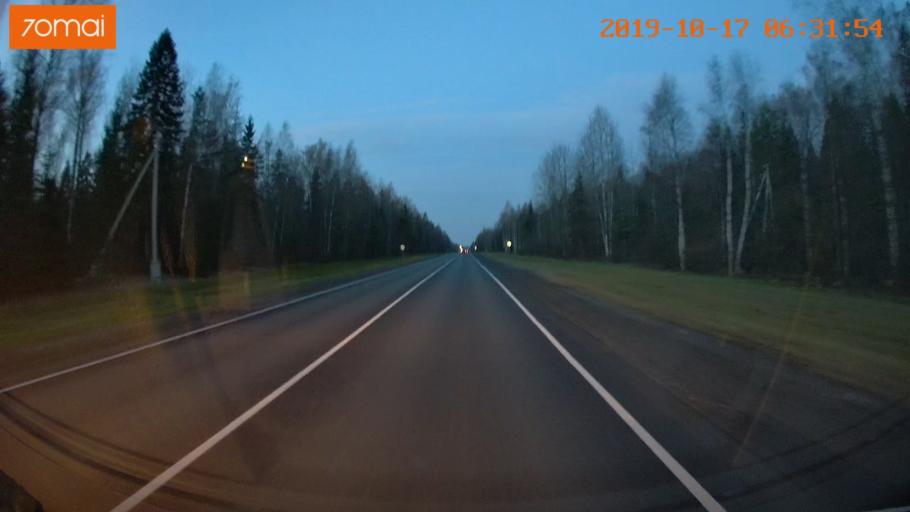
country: RU
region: Ivanovo
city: Novoye Leushino
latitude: 56.7242
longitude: 40.6885
